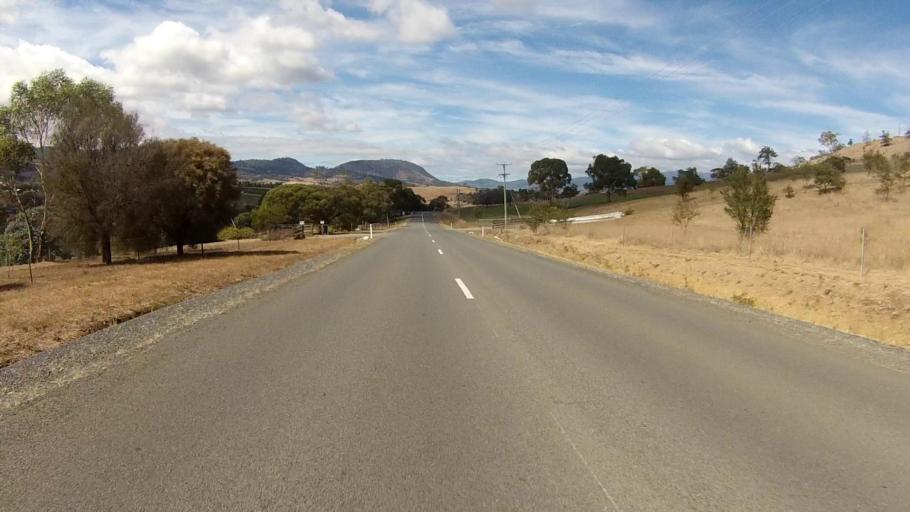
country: AU
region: Tasmania
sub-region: Brighton
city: Old Beach
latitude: -42.7311
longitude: 147.2887
